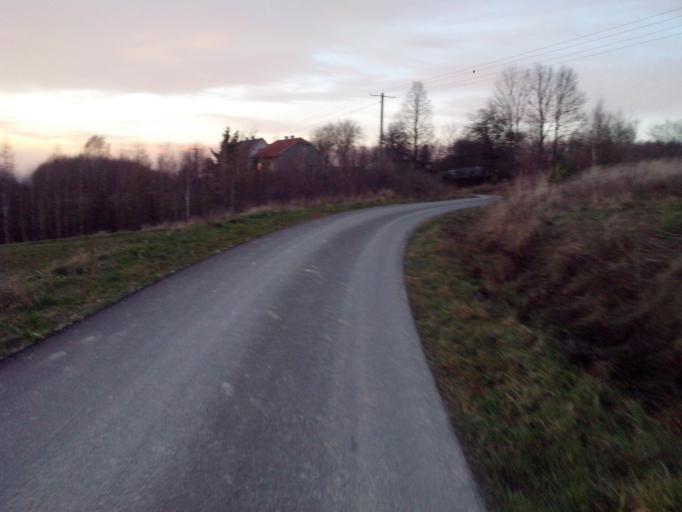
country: PL
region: Subcarpathian Voivodeship
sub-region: Powiat strzyzowski
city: Strzyzow
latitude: 49.8500
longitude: 21.8267
